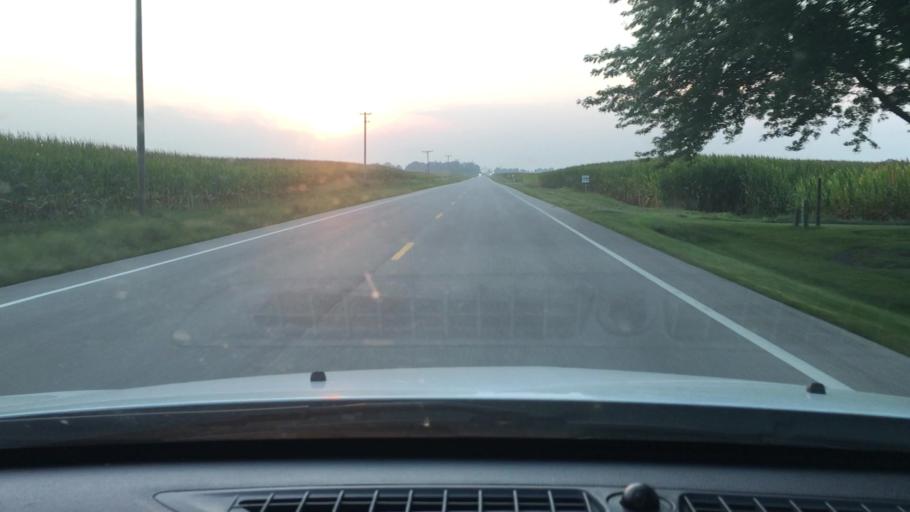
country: US
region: Illinois
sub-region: DeKalb County
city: Waterman
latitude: 41.8489
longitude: -88.8057
